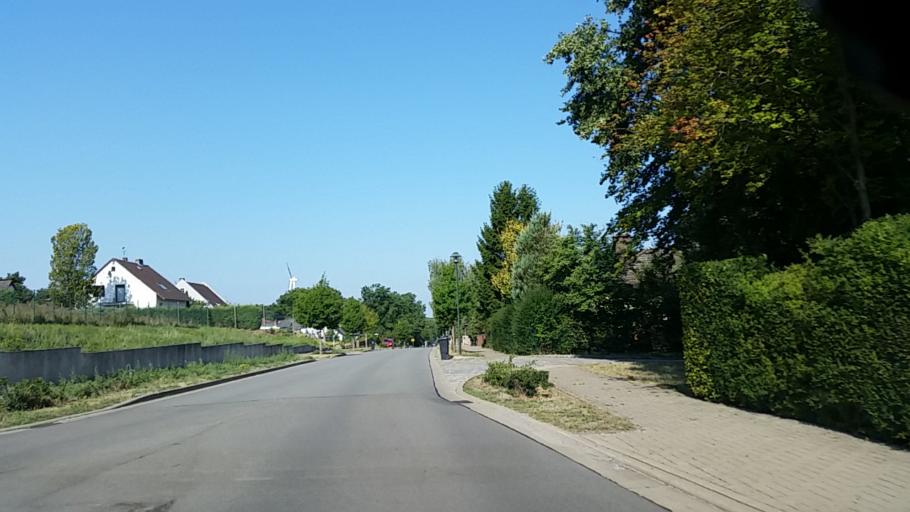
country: DE
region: Lower Saxony
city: Barwedel
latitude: 52.5244
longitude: 10.7718
